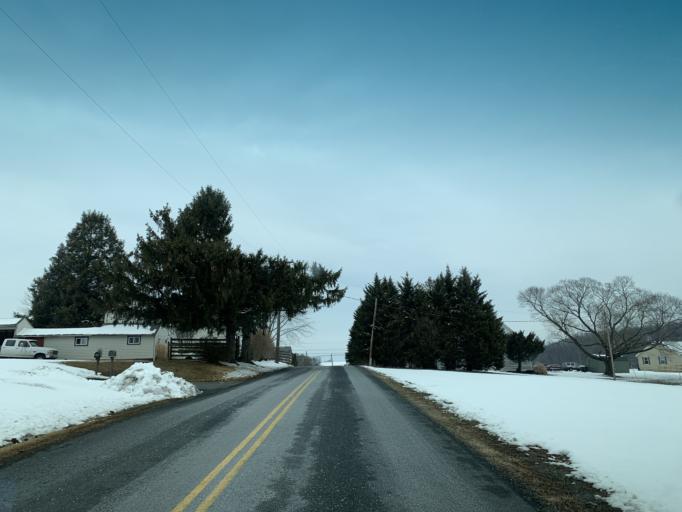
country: US
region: Pennsylvania
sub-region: York County
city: Susquehanna Trails
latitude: 39.7201
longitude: -76.4152
